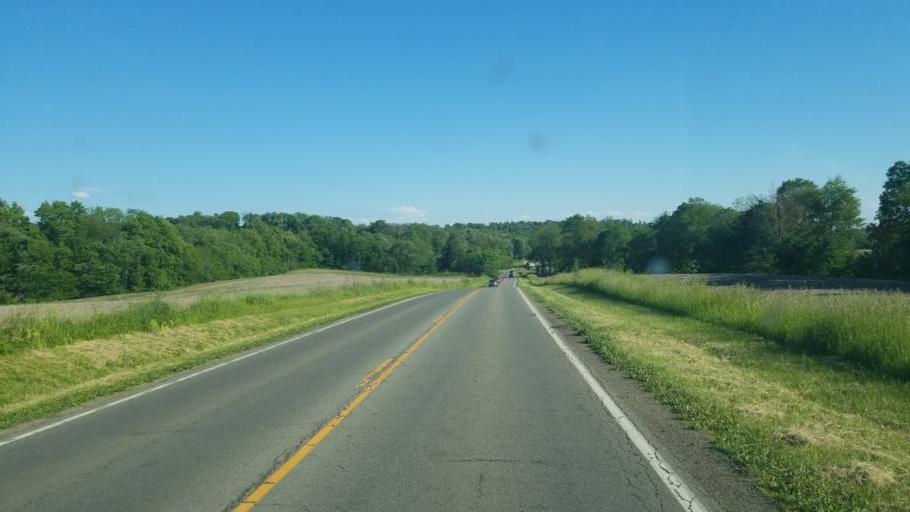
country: US
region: Ohio
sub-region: Richland County
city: Lexington
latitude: 40.7151
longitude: -82.5822
